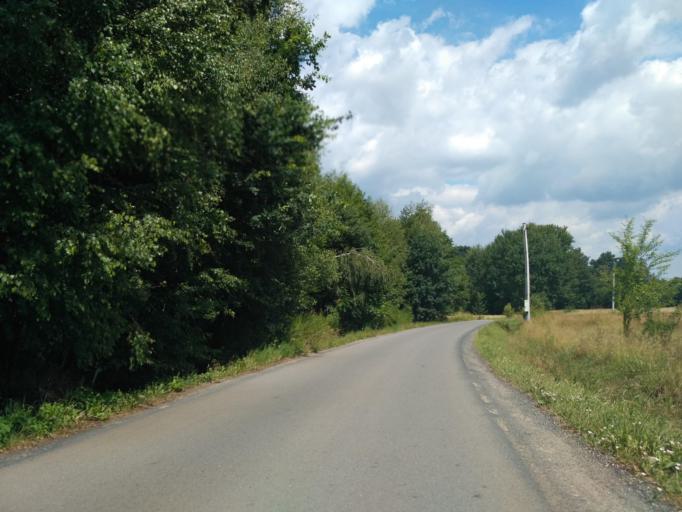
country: PL
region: Subcarpathian Voivodeship
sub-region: Powiat debicki
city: Slotowa
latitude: 49.9595
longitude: 21.2936
